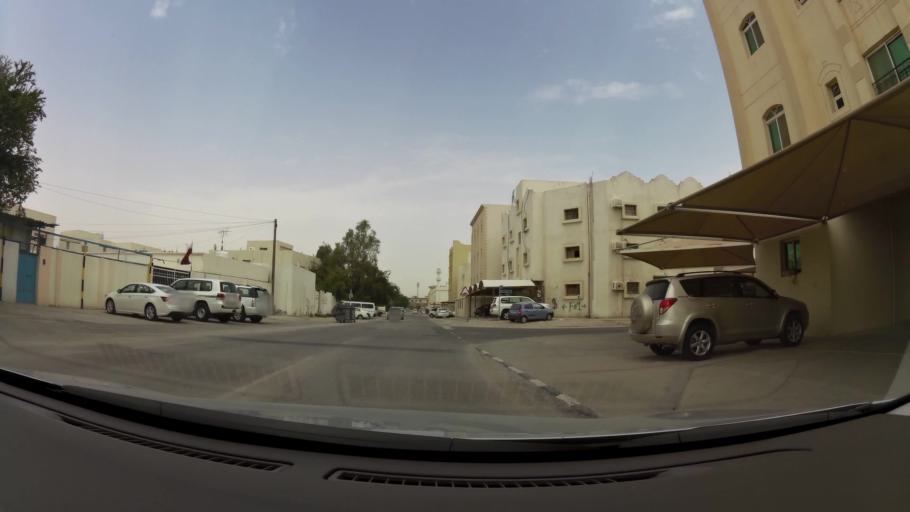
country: QA
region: Baladiyat ad Dawhah
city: Doha
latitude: 25.3053
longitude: 51.4929
